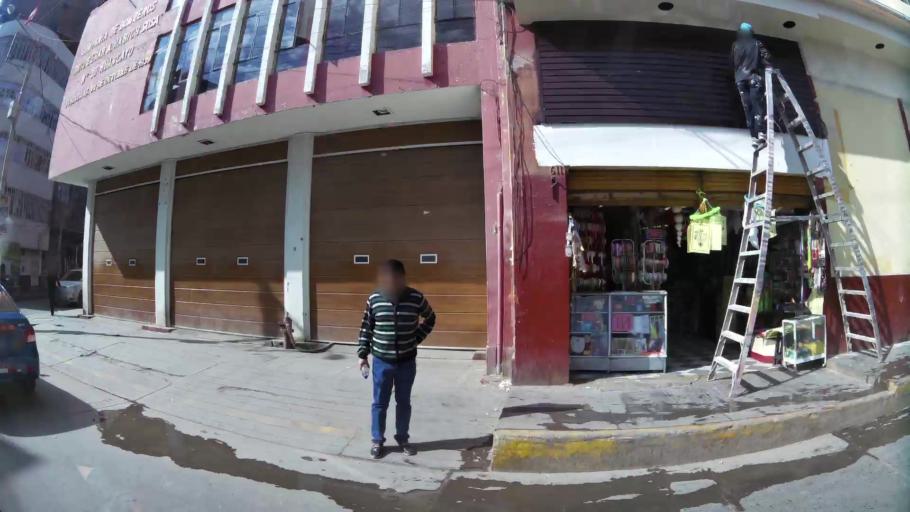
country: PE
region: Junin
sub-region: Provincia de Huancayo
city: Huancayo
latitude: -12.0696
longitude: -75.2085
